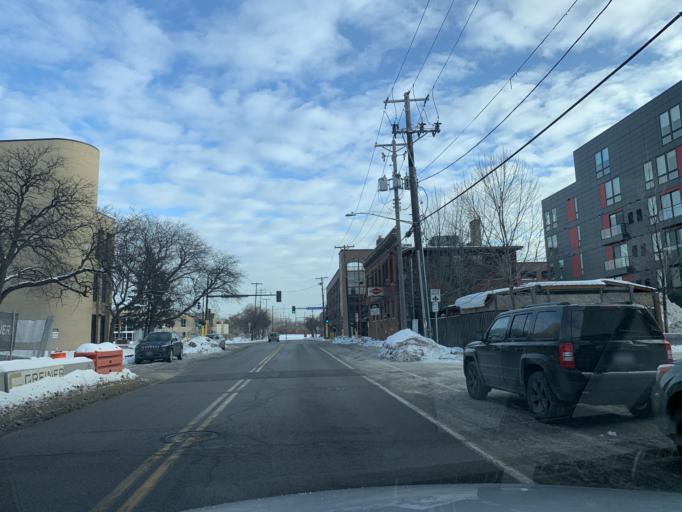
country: US
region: Minnesota
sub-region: Hennepin County
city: Minneapolis
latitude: 44.9898
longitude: -93.2813
